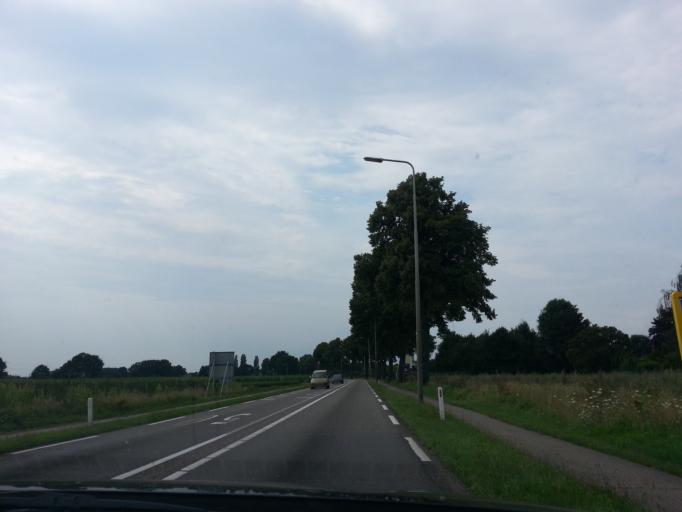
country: NL
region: Limburg
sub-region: Gemeente Leudal
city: Heythuysen
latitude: 51.2218
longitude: 5.8806
